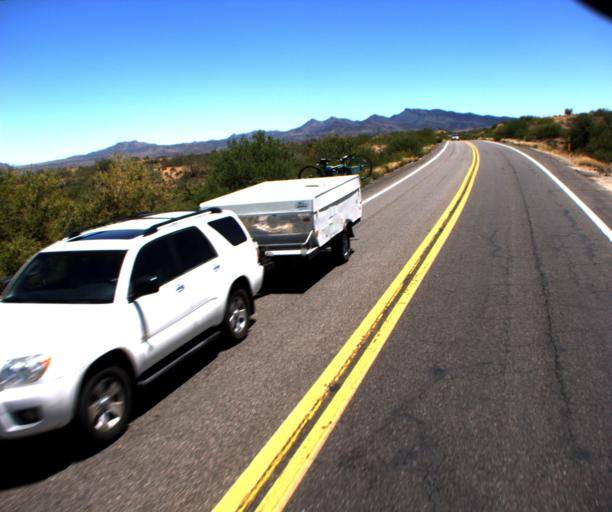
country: US
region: Arizona
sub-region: Gila County
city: Globe
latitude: 33.3509
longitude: -110.7334
